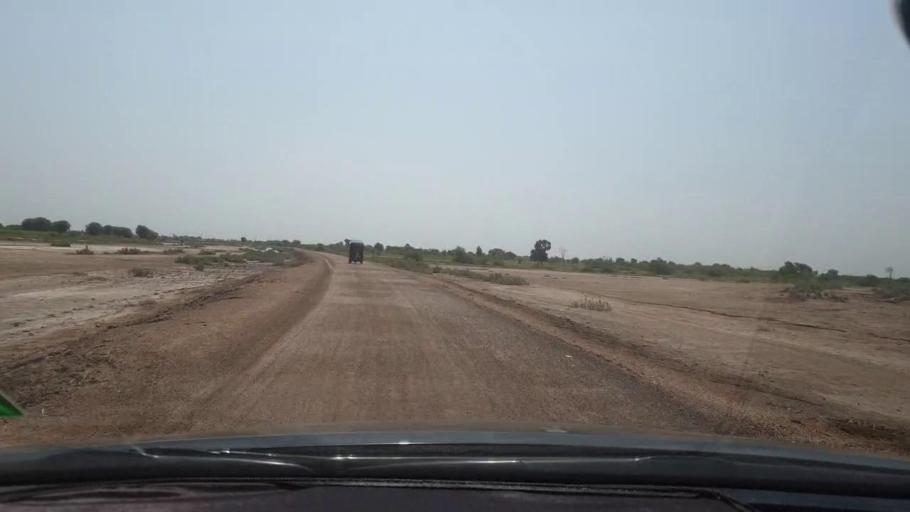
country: PK
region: Sindh
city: Tando Bago
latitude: 24.7943
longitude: 69.1674
